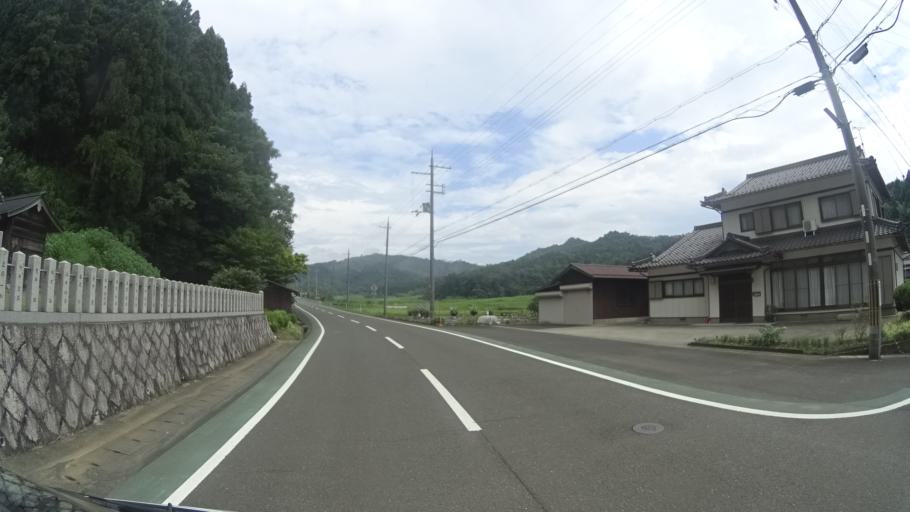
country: JP
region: Kyoto
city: Ayabe
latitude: 35.3576
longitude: 135.3222
